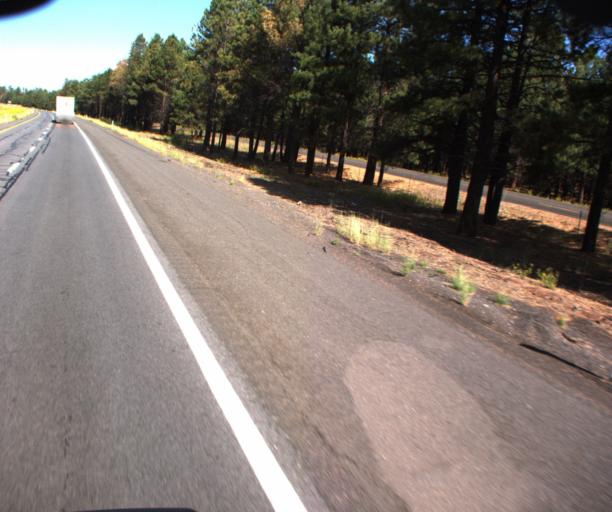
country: US
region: Arizona
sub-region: Coconino County
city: Parks
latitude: 35.2472
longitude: -111.8463
